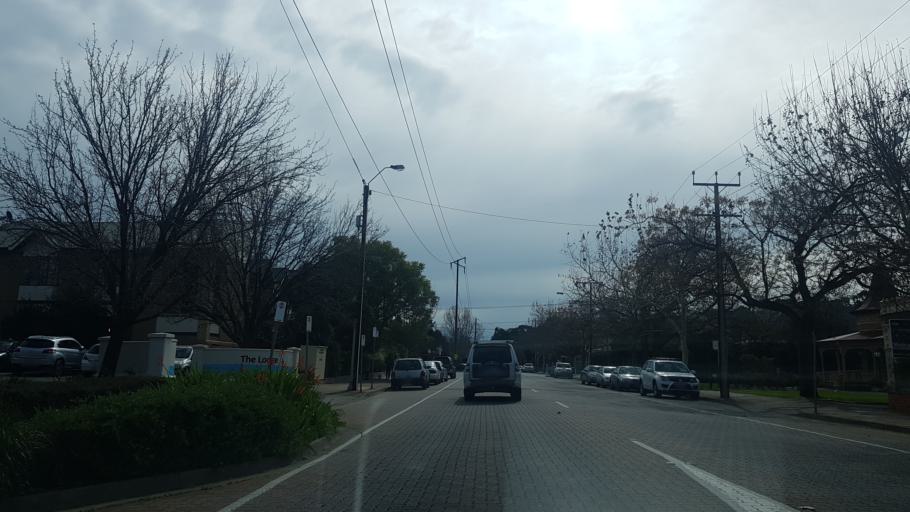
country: AU
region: South Australia
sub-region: Unley
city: Unley
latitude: -34.9459
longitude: 138.5994
